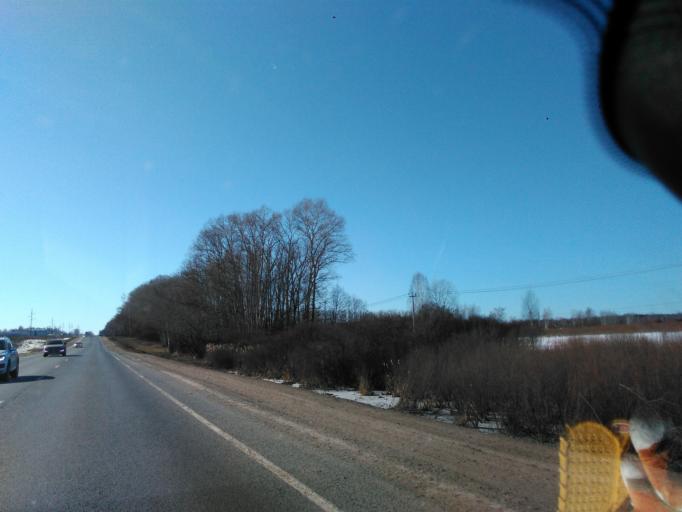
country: RU
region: Moskovskaya
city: Yermolino
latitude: 56.1359
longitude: 37.4218
